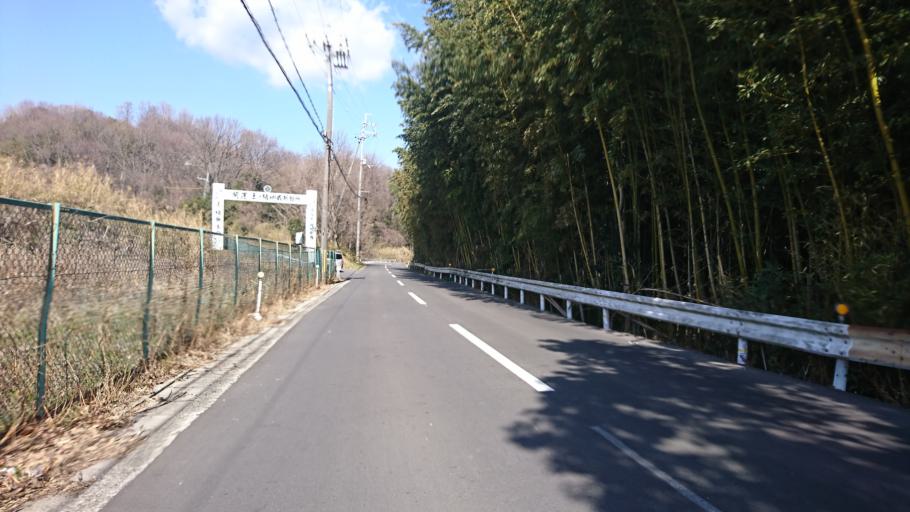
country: JP
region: Hyogo
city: Kakogawacho-honmachi
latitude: 34.8331
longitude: 134.8228
